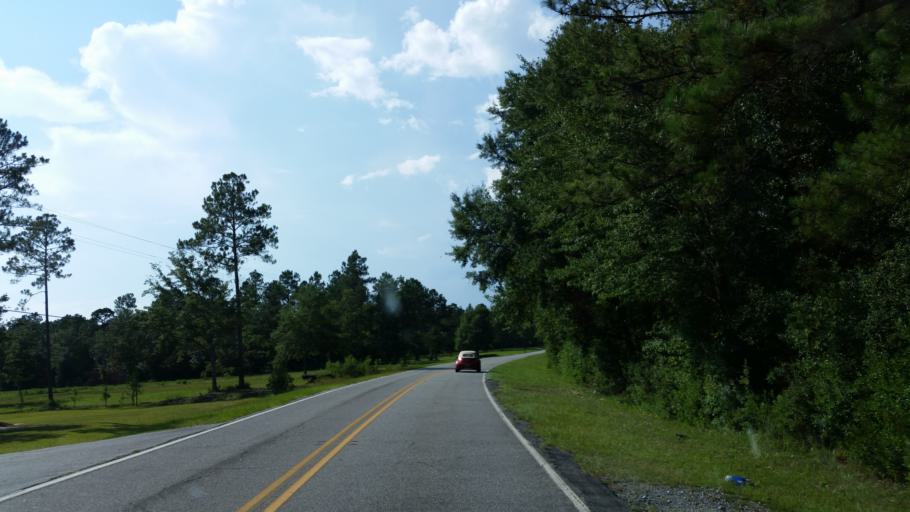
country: US
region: Georgia
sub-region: Lowndes County
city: Hahira
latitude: 30.9033
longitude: -83.3806
